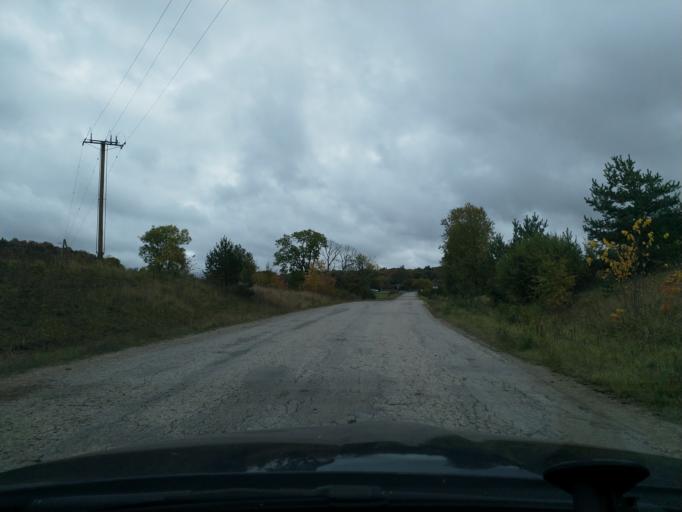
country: LV
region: Alsunga
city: Alsunga
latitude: 57.0234
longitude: 21.6860
